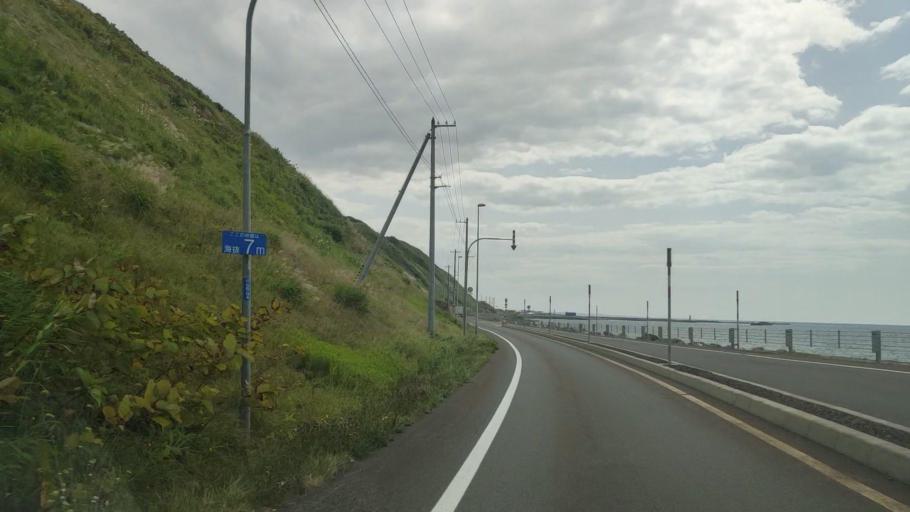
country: JP
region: Hokkaido
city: Rumoi
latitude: 44.5452
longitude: 141.7670
